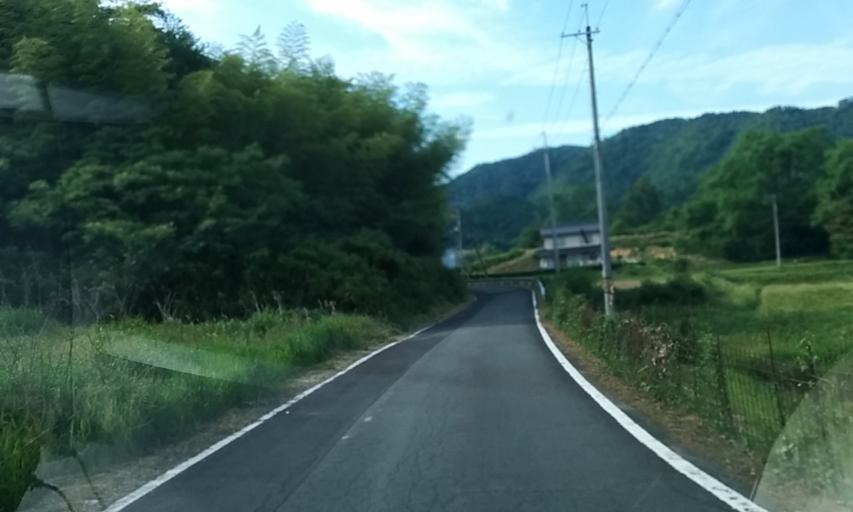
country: JP
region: Kyoto
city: Ayabe
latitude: 35.3596
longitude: 135.2064
